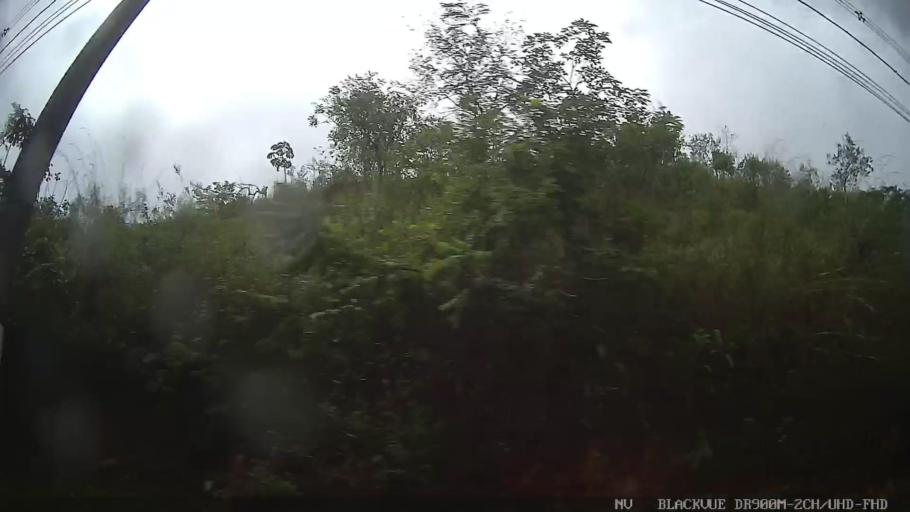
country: BR
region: Sao Paulo
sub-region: Pedreira
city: Pedreira
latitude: -22.7402
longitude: -46.9204
